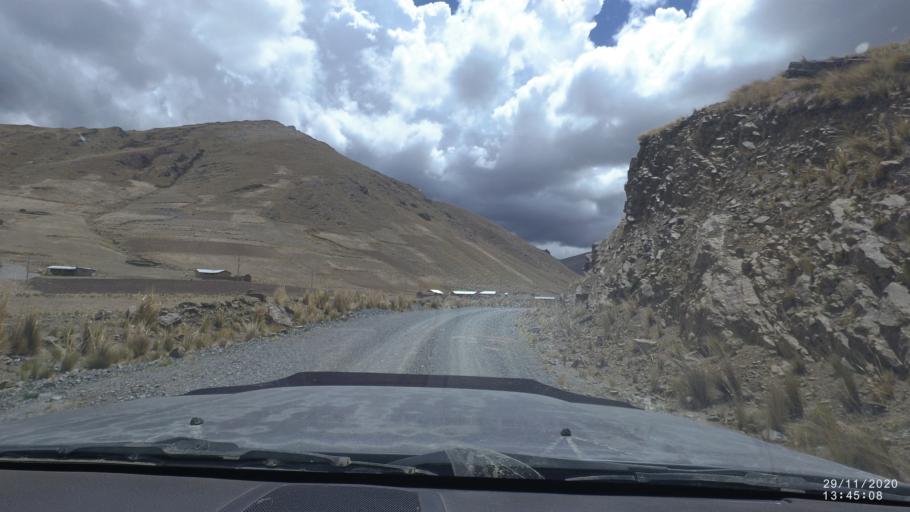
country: BO
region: Cochabamba
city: Cochabamba
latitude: -17.1485
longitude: -66.3192
